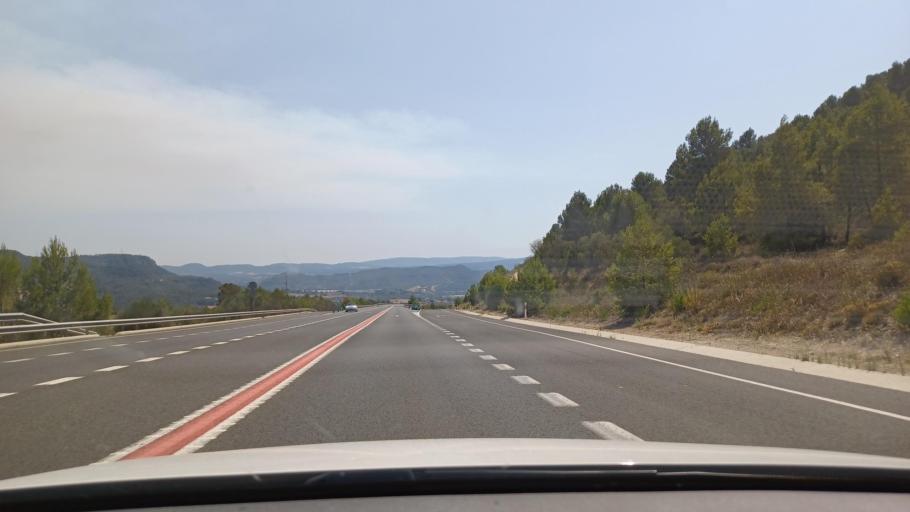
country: ES
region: Catalonia
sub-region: Provincia de Barcelona
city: Castelloli
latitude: 41.6053
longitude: 1.6758
